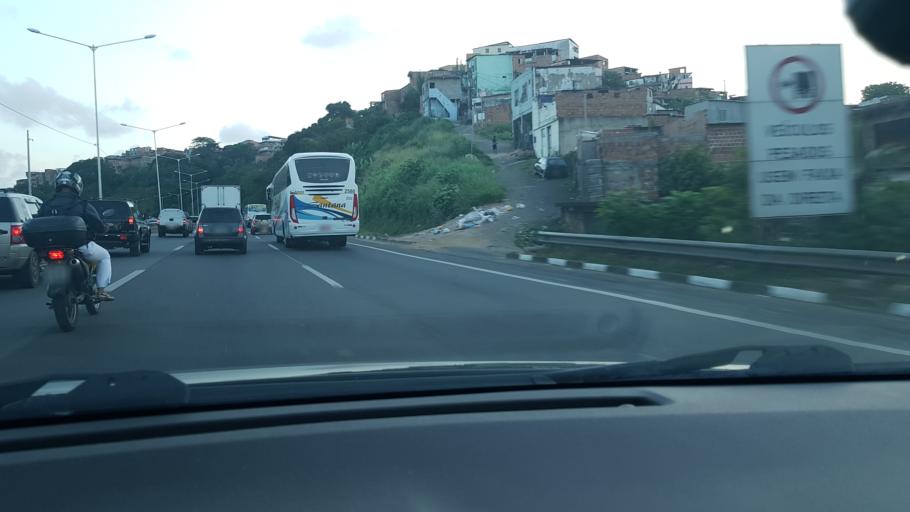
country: BR
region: Bahia
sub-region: Salvador
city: Salvador
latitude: -12.9335
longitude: -38.4717
